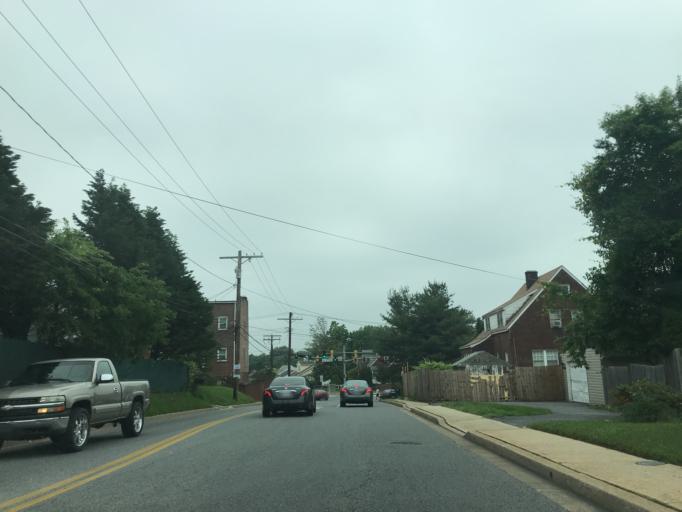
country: US
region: Maryland
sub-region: Baltimore County
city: Charlestown
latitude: 39.2682
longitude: -76.6914
